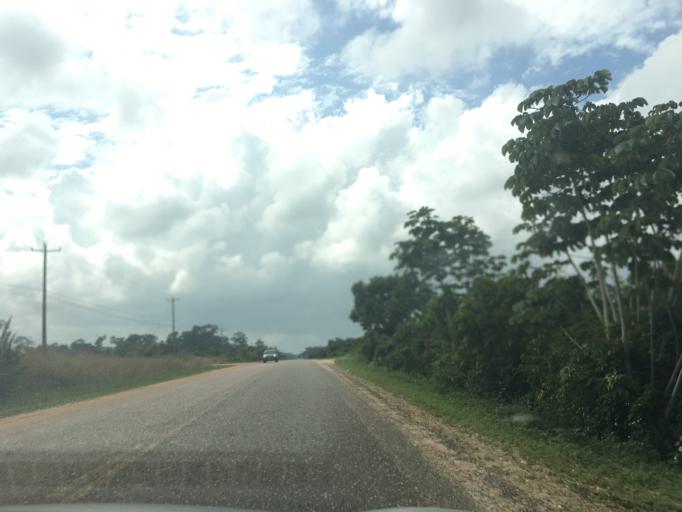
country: BZ
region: Stann Creek
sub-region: Dangriga
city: Dangriga
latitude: 16.9712
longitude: -88.3032
